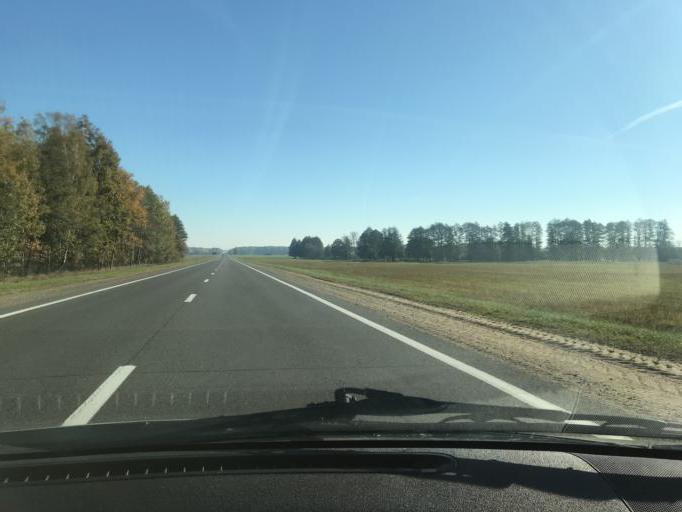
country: BY
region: Brest
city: Ivanava
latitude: 52.1560
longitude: 25.6985
